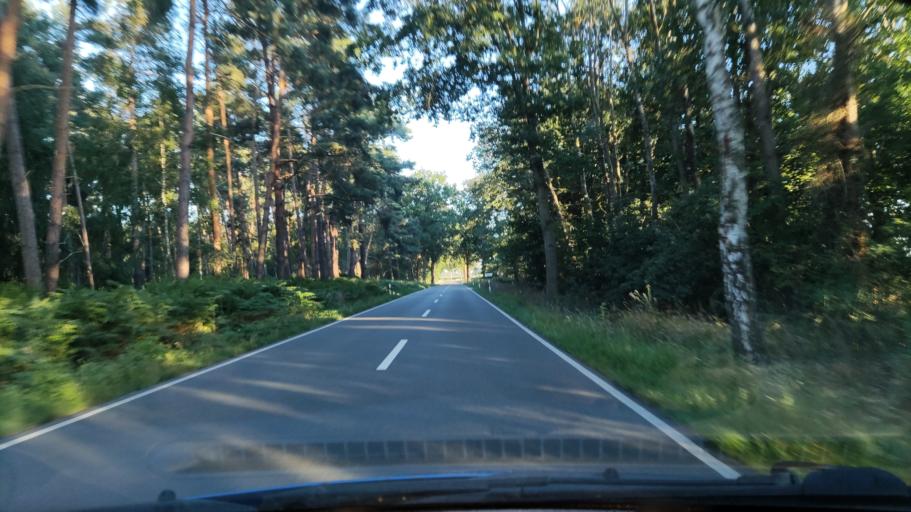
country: DE
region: Lower Saxony
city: Luechow
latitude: 53.0169
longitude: 11.1486
